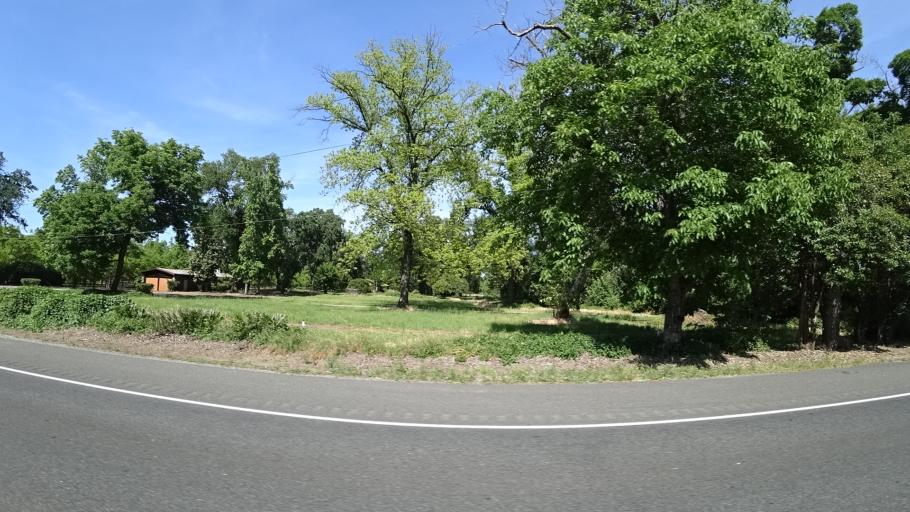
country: US
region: California
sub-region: Tehama County
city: Red Bluff
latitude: 40.1722
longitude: -122.1647
